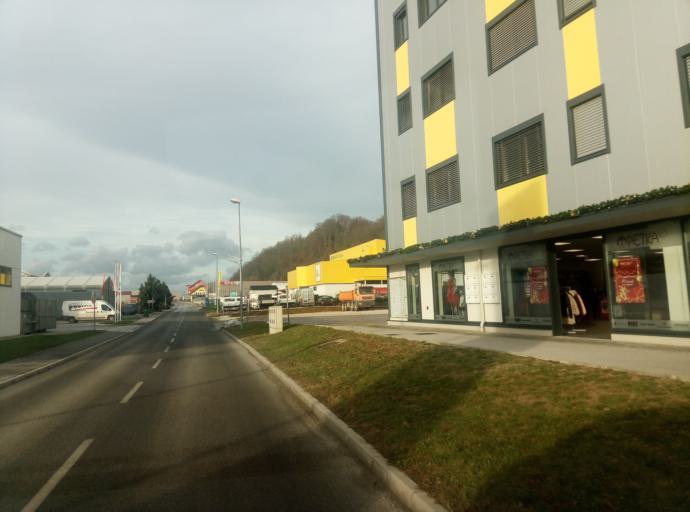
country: SI
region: Sentjur pri Celju
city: Sentjur
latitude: 46.2147
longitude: 15.3896
